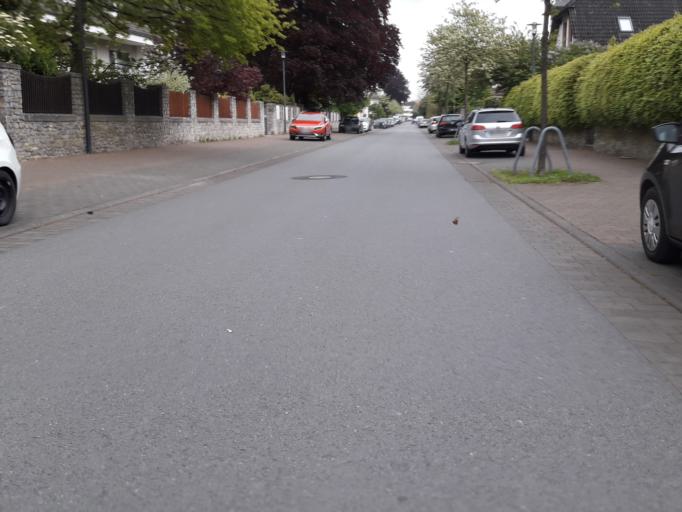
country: DE
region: North Rhine-Westphalia
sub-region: Regierungsbezirk Detmold
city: Detmold
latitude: 51.9391
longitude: 8.8640
